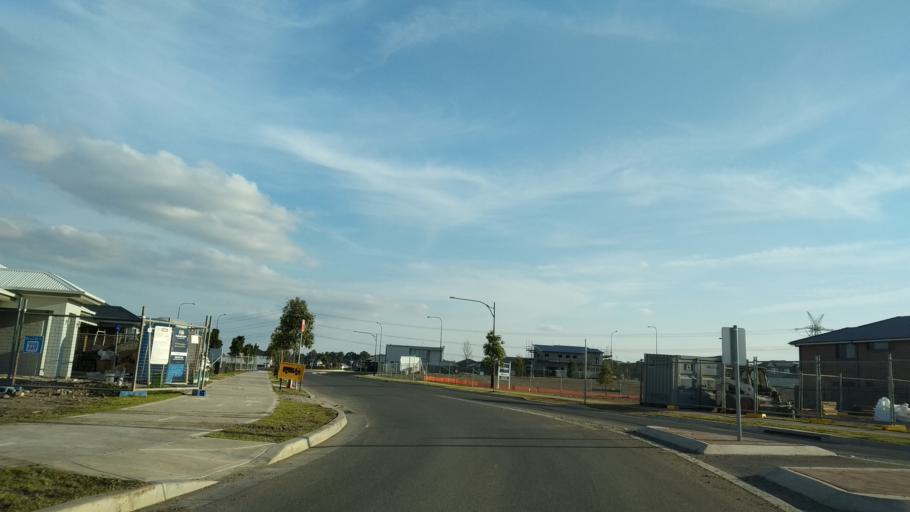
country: AU
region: New South Wales
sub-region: Penrith Municipality
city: Werrington County
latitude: -33.7346
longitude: 150.7542
